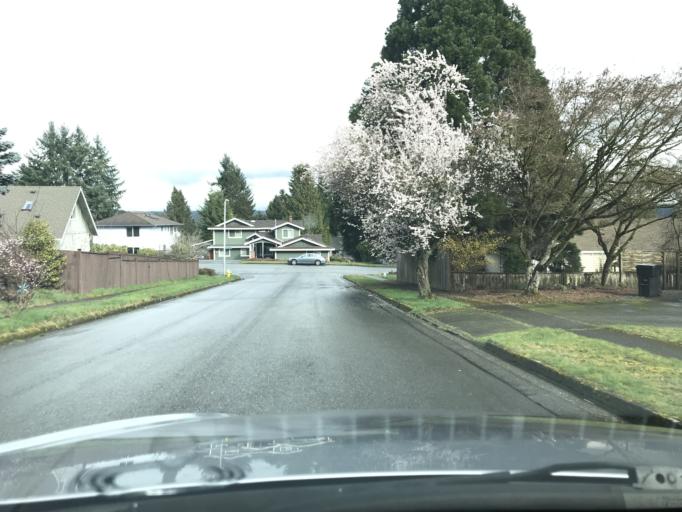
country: US
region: Washington
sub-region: King County
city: Redmond
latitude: 47.6564
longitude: -122.1294
